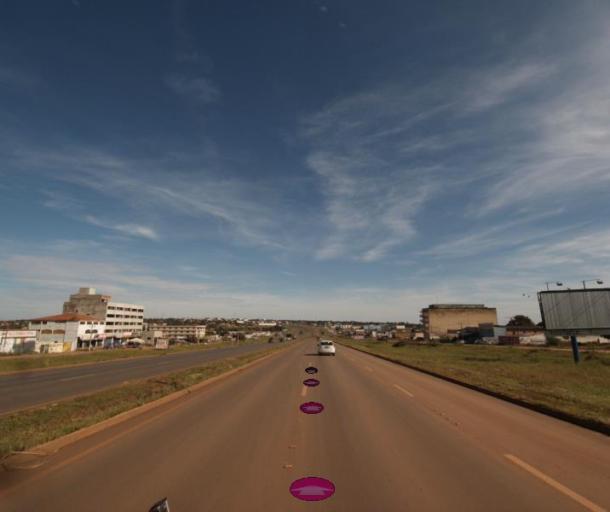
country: BR
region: Federal District
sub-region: Brasilia
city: Brasilia
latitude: -15.7452
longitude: -48.2664
